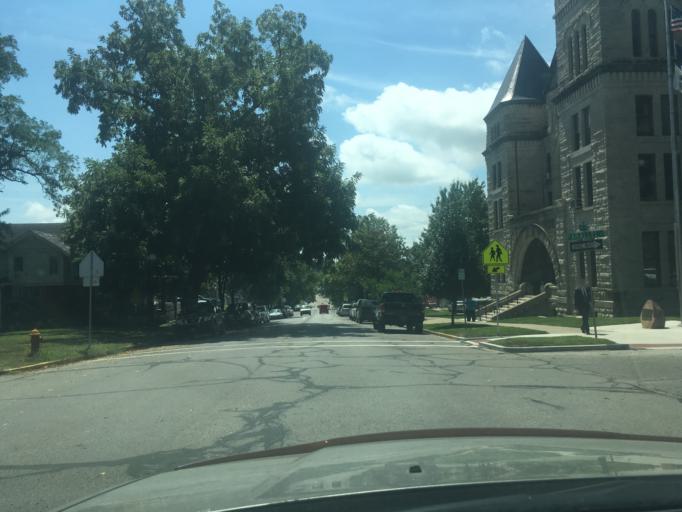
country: US
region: Kansas
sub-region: Atchison County
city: Atchison
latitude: 39.5663
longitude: -95.1191
